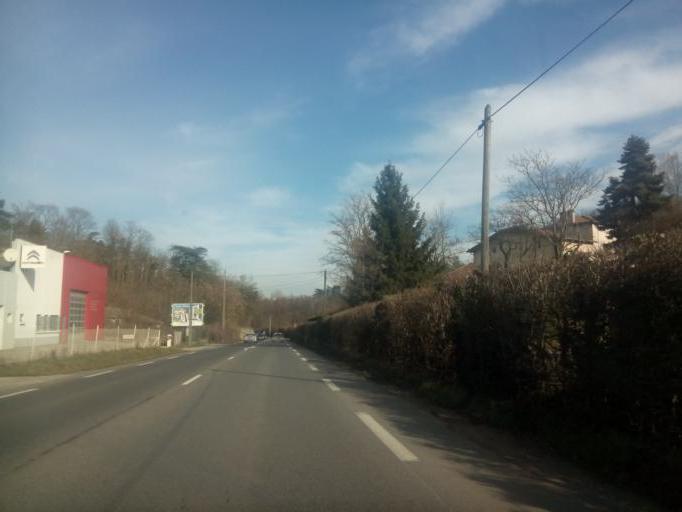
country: FR
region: Rhone-Alpes
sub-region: Departement du Rhone
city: Francheville
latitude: 45.7136
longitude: 4.7741
